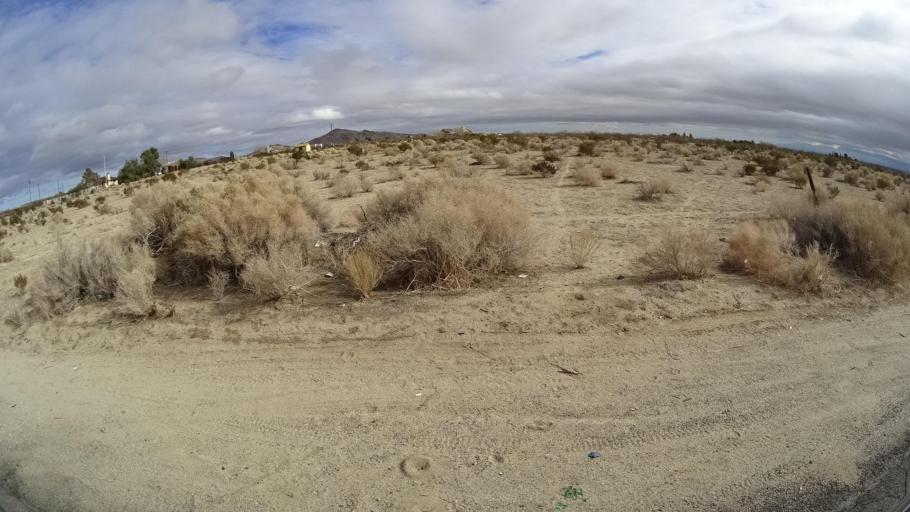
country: US
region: California
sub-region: Kern County
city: Rosamond
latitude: 34.8731
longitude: -118.2292
